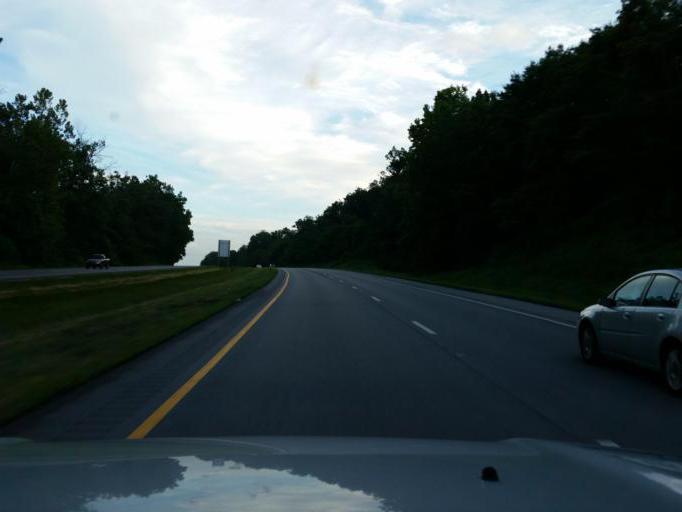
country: US
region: Maryland
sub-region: Frederick County
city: Thurmont
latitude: 39.5999
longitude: -77.4301
